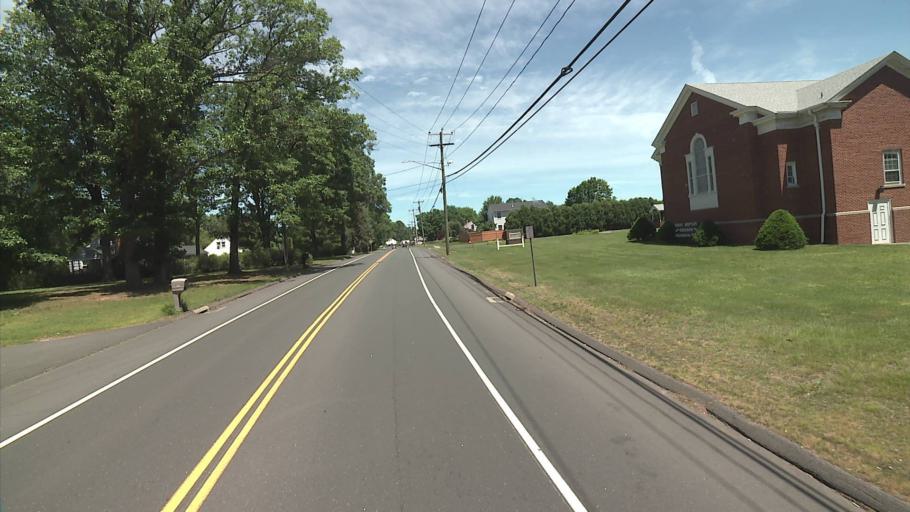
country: US
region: Connecticut
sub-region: New Haven County
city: Meriden
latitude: 41.5822
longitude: -72.8693
